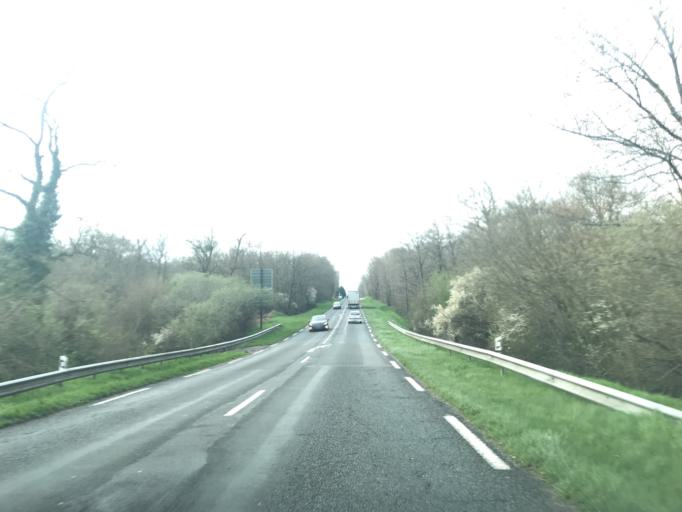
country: FR
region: Centre
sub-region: Departement du Loiret
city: Nevoy
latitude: 47.7272
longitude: 2.5774
